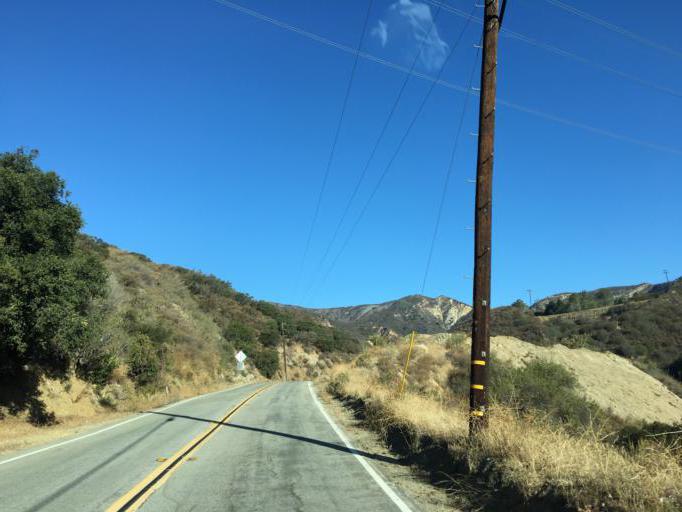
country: US
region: California
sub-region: Los Angeles County
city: San Fernando
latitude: 34.3276
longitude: -118.3399
